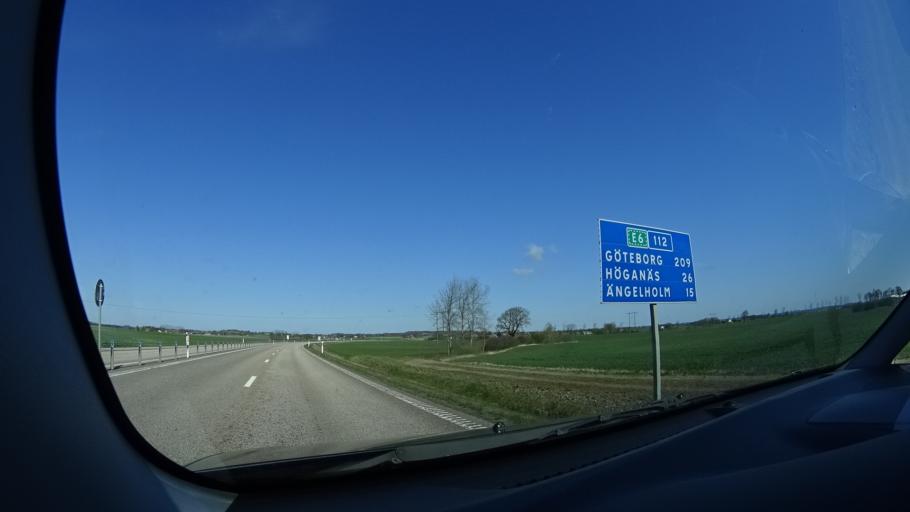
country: SE
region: Skane
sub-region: Astorps Kommun
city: Astorp
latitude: 56.1499
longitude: 12.9256
